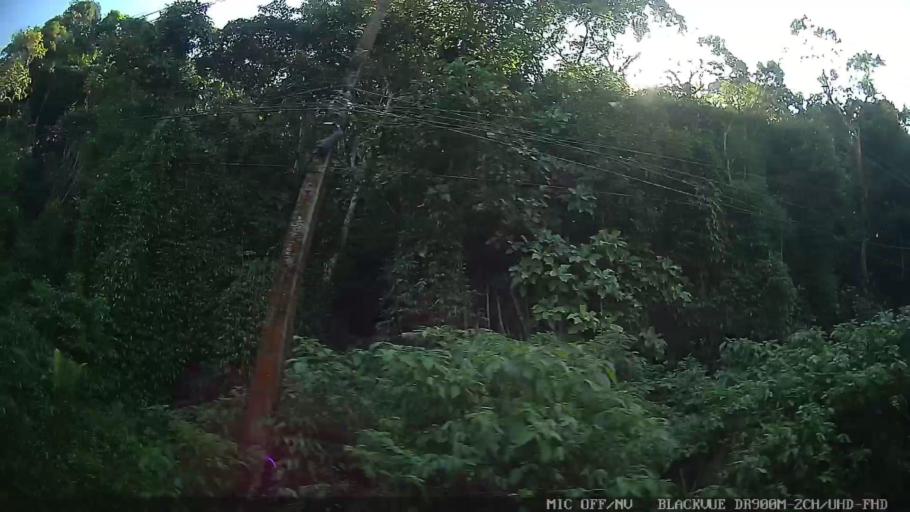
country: BR
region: Sao Paulo
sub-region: Santos
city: Santos
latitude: -23.9982
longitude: -46.3105
